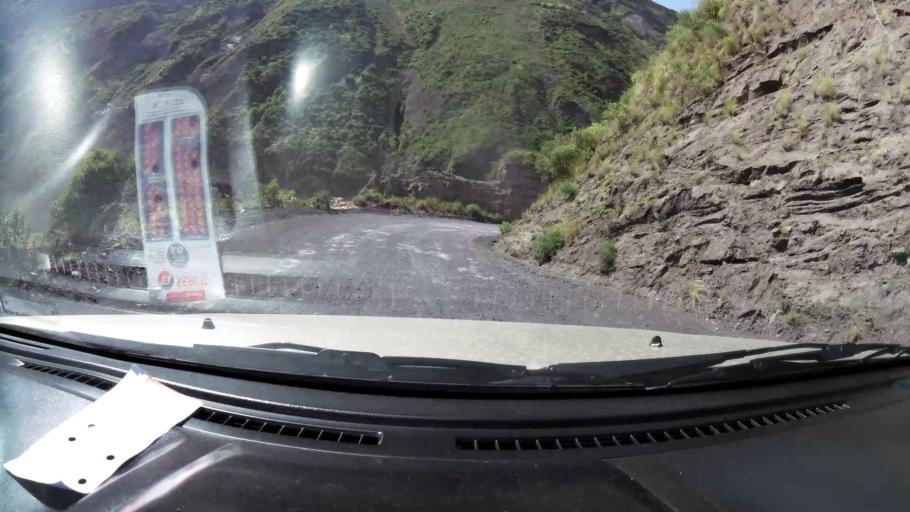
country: EC
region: Tungurahua
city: Banos
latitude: -1.4789
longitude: -78.5129
